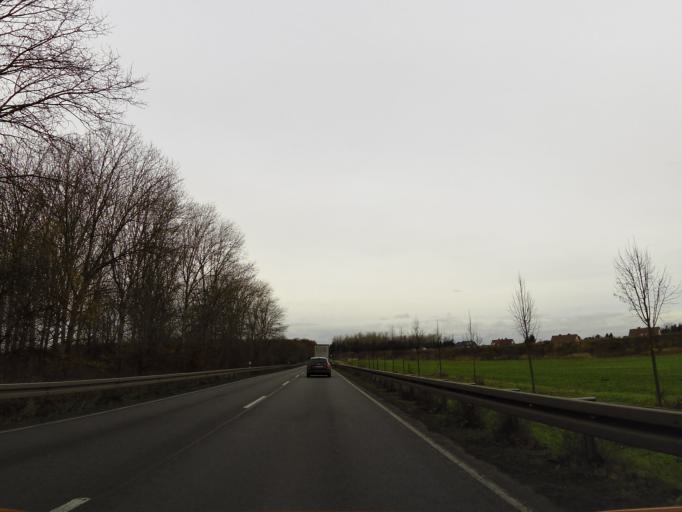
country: DE
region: Saxony-Anhalt
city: Salzwedel
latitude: 52.8340
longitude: 11.1841
